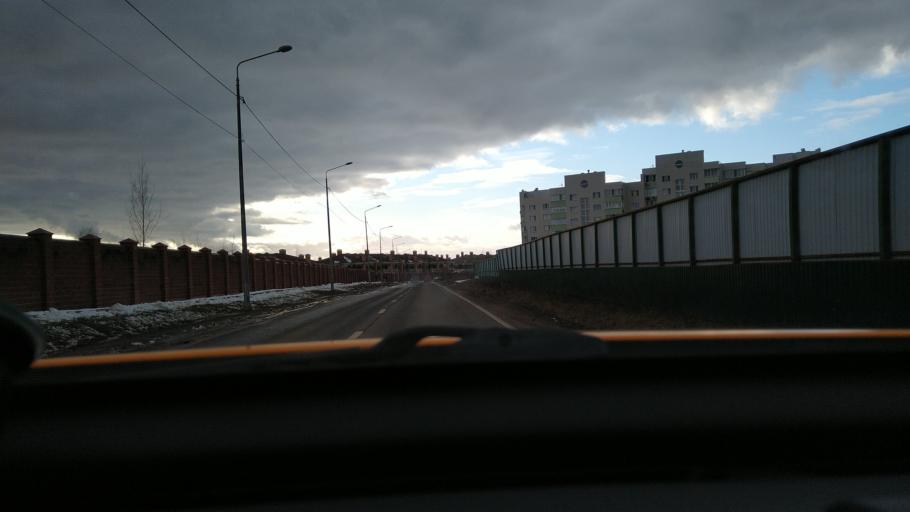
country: RU
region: Moskovskaya
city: Petrovo-Dal'neye
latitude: 55.7721
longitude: 37.2106
